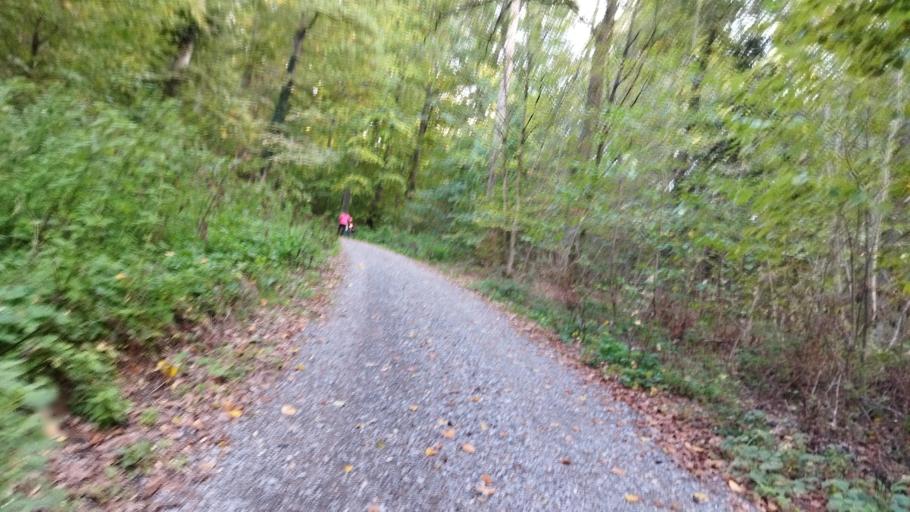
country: DE
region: Baden-Wuerttemberg
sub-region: Karlsruhe Region
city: Sulzfeld
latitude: 49.0907
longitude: 8.8941
